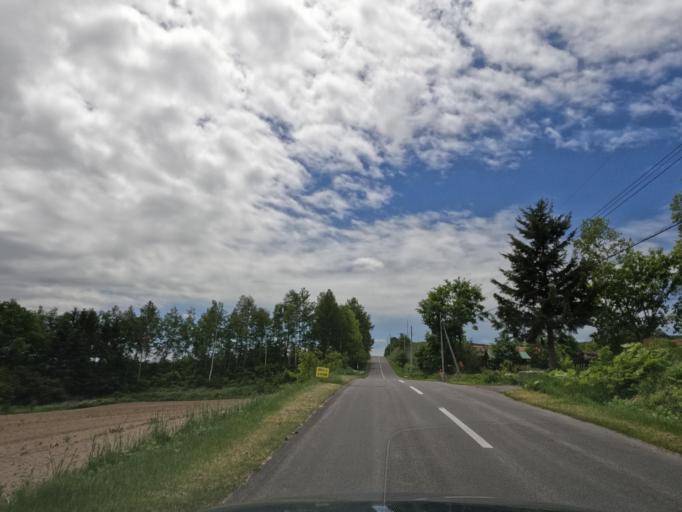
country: JP
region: Hokkaido
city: Shimo-furano
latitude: 43.5226
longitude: 142.4323
